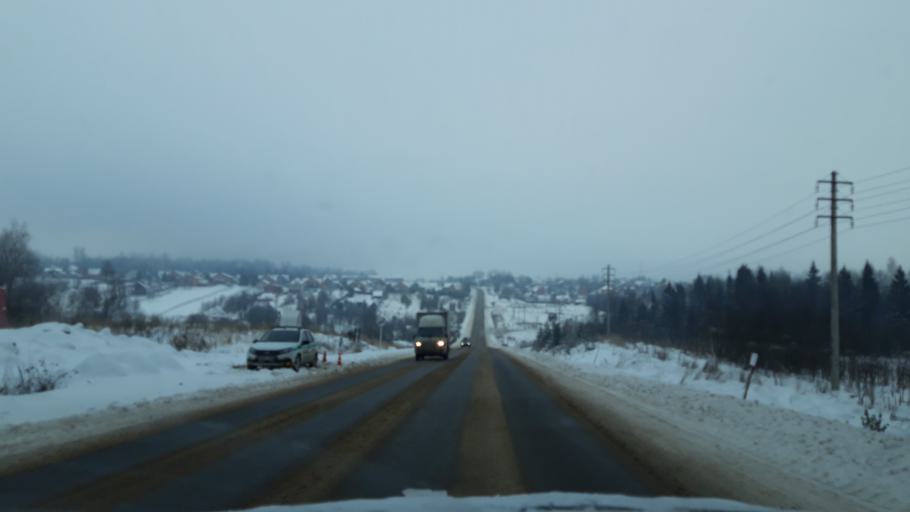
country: RU
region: Moskovskaya
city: Avtopoligon
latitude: 56.2665
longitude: 37.3310
